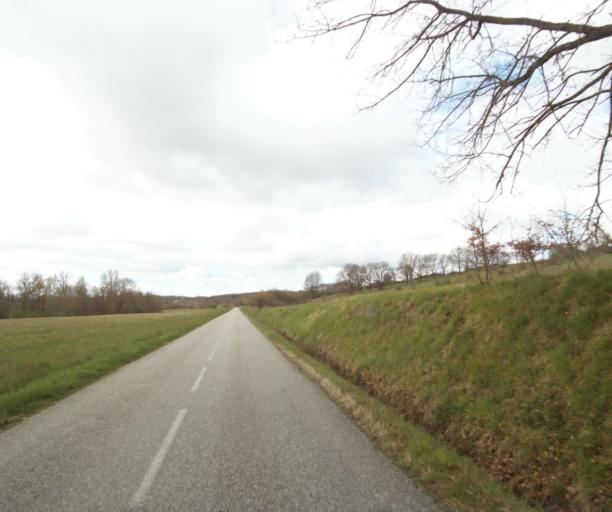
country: FR
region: Midi-Pyrenees
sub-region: Departement de l'Ariege
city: Saverdun
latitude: 43.2144
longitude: 1.5261
